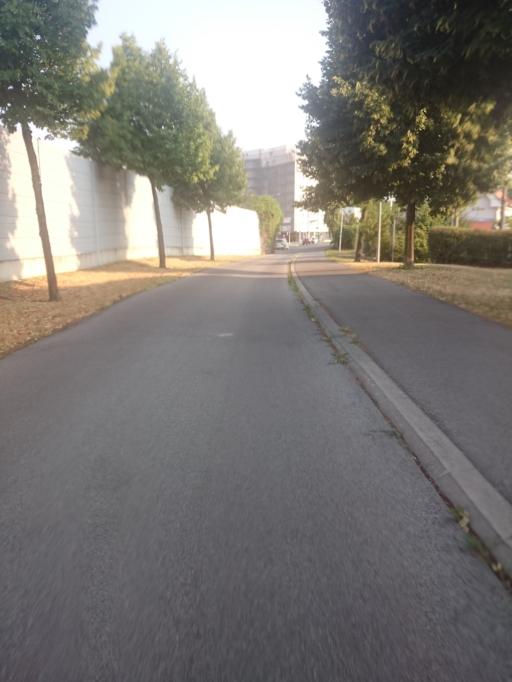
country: AT
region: Lower Austria
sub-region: Politischer Bezirk Wien-Umgebung
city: Gerasdorf bei Wien
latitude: 48.2533
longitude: 16.4275
